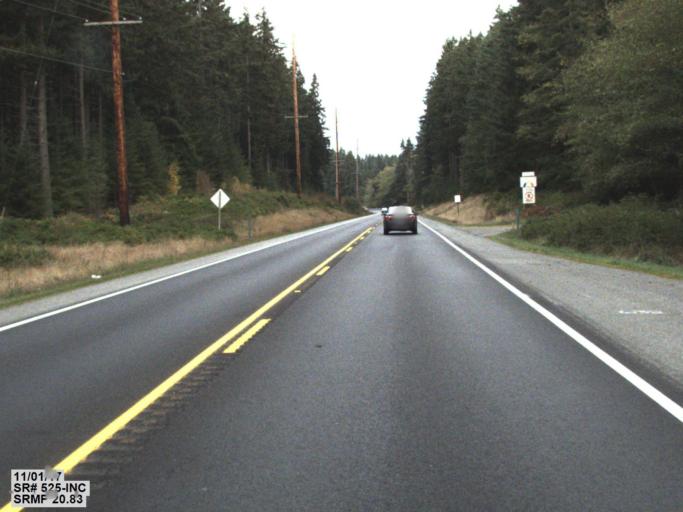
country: US
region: Washington
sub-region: Island County
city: Freeland
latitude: 48.0381
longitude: -122.5647
